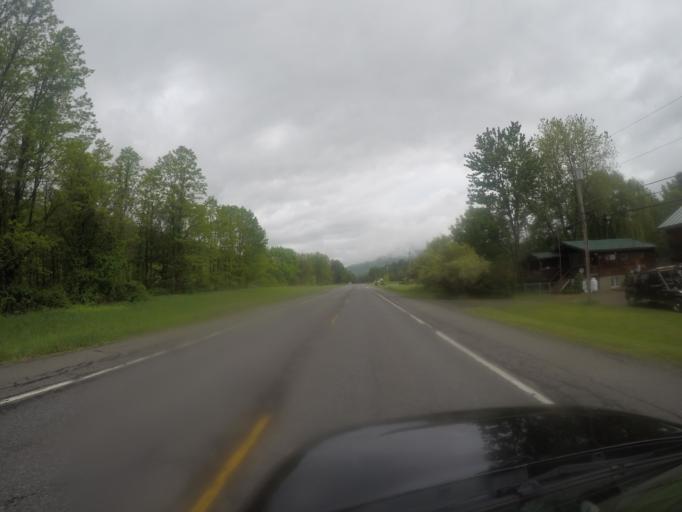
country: US
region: New York
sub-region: Ulster County
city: Shokan
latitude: 42.0317
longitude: -74.2747
